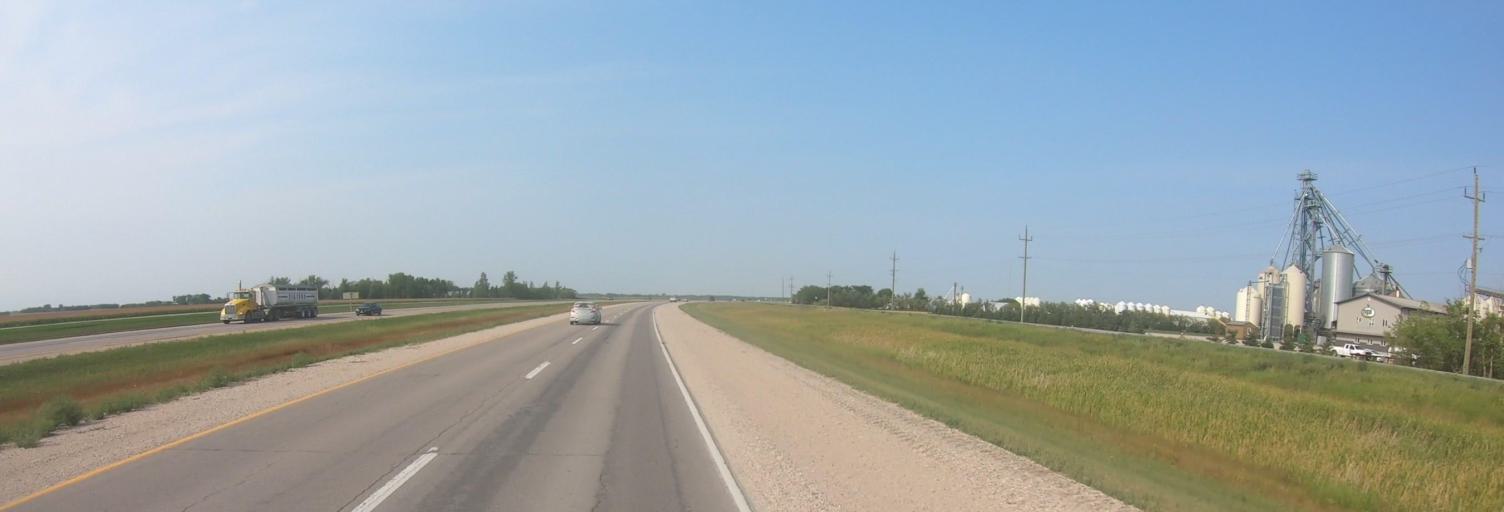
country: CA
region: Manitoba
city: Steinbach
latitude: 49.6348
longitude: -96.6869
